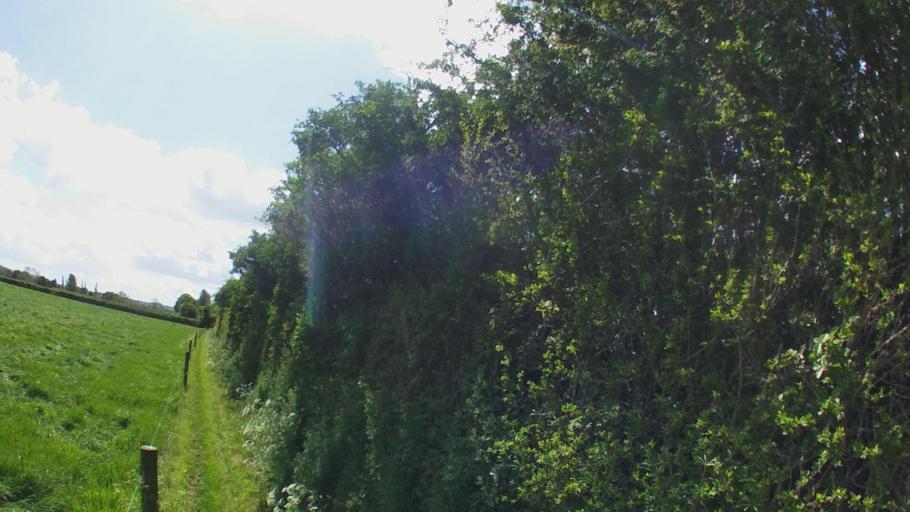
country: IE
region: Leinster
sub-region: Kilkenny
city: Thomastown
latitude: 52.5989
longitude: -7.1648
